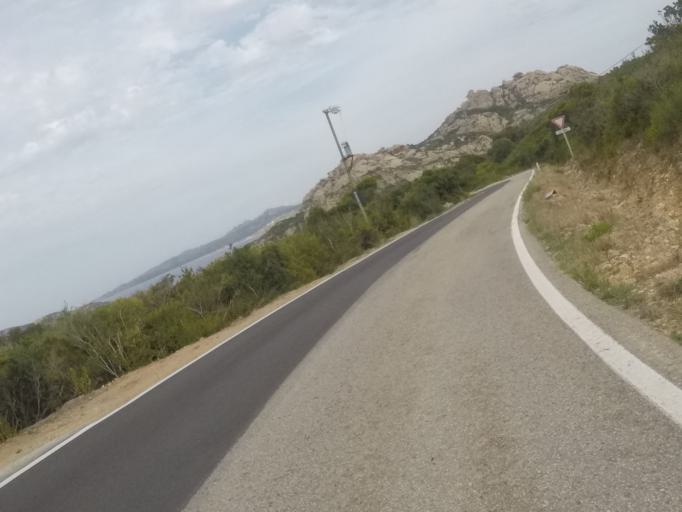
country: IT
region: Sardinia
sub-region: Provincia di Olbia-Tempio
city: Palau
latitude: 41.1712
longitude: 9.4024
